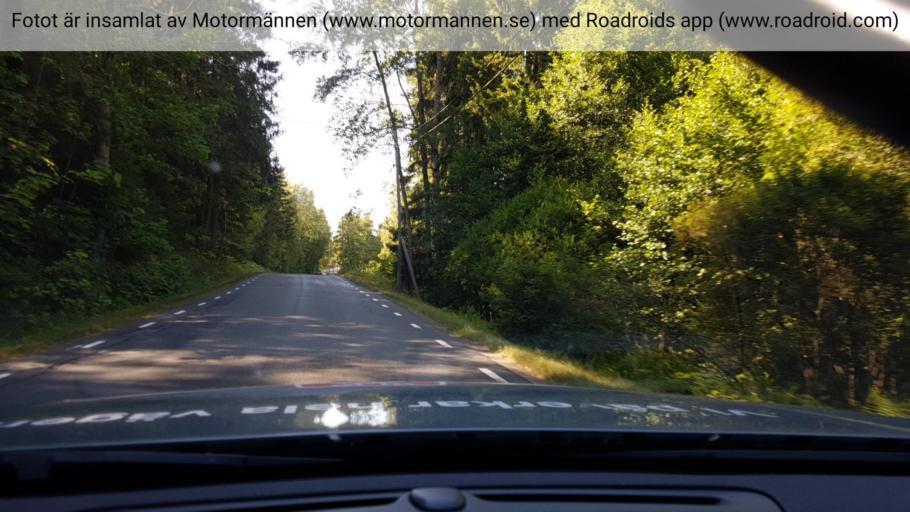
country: SE
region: Vaestra Goetaland
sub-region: Karlsborgs Kommun
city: Molltorp
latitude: 58.6667
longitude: 14.3773
